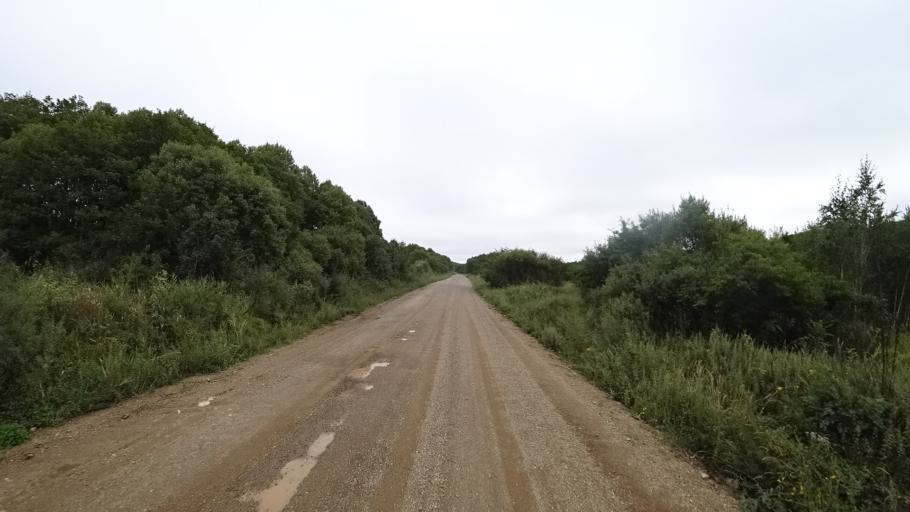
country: RU
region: Primorskiy
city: Ivanovka
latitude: 44.0558
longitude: 132.4799
